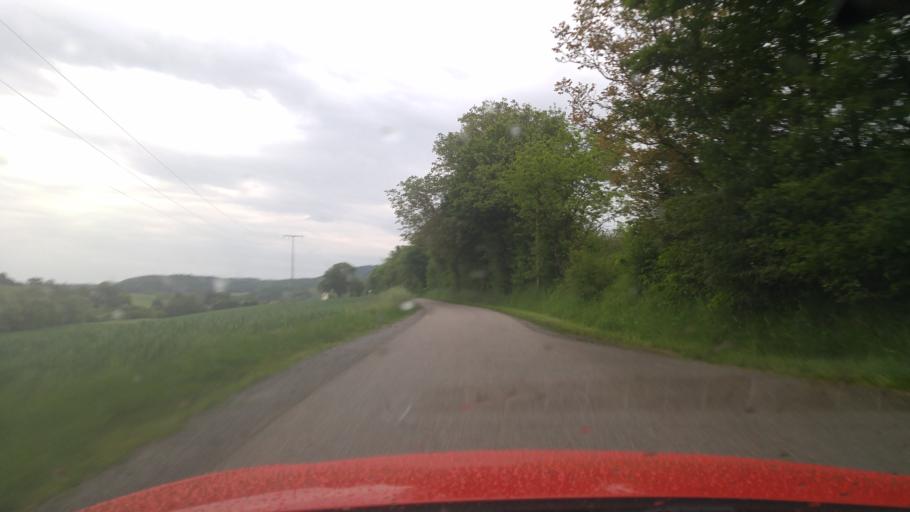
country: DE
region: Baden-Wuerttemberg
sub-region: Regierungsbezirk Stuttgart
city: Gemmingen
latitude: 49.1114
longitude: 8.9755
